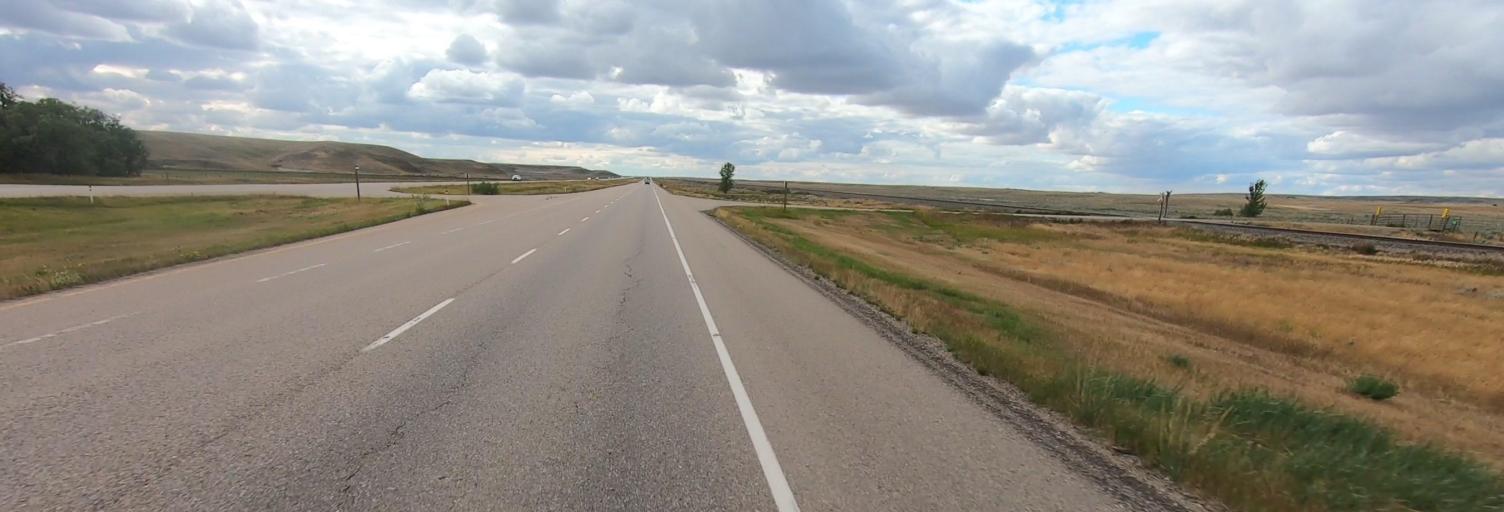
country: CA
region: Alberta
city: Medicine Hat
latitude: 49.9431
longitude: -110.1913
